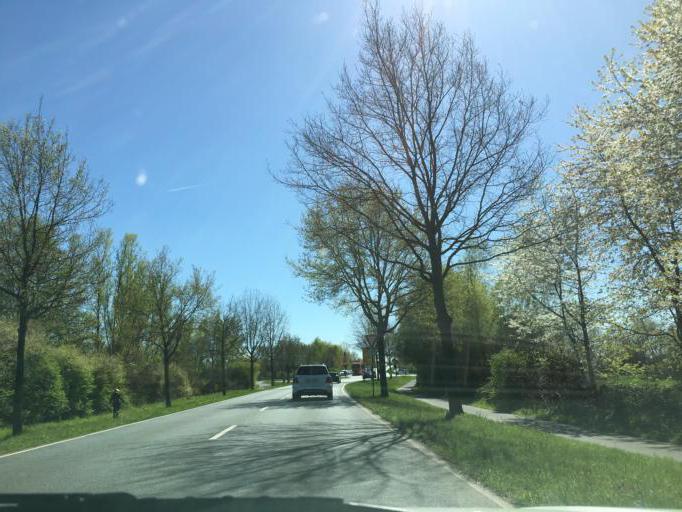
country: DE
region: Hesse
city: Obertshausen
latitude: 50.0721
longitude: 8.8724
